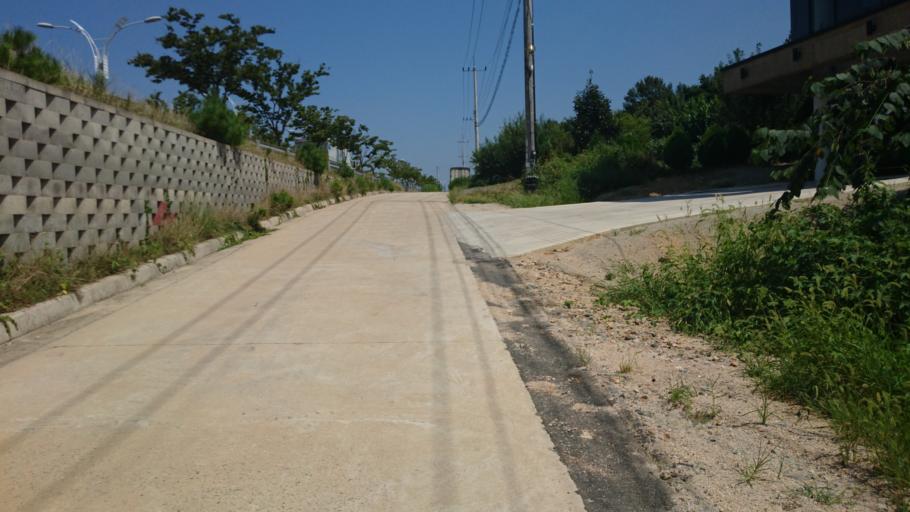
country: KR
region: Gyeongsangbuk-do
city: Gyeongsan-si
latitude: 35.8295
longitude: 128.6707
